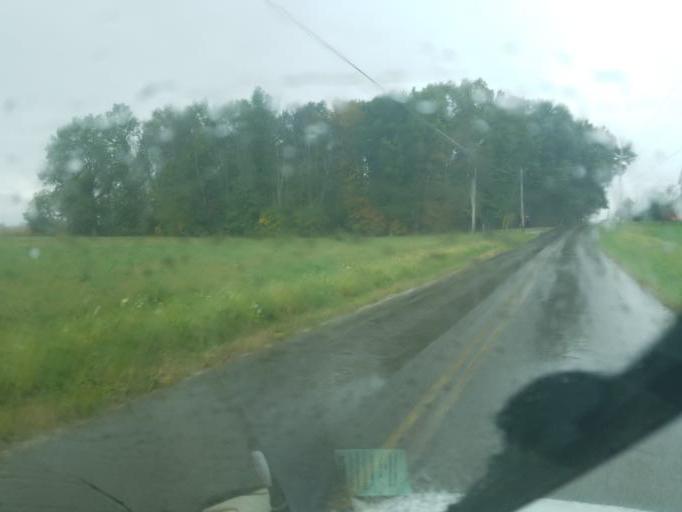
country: US
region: Ohio
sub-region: Wayne County
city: Shreve
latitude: 40.6453
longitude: -82.0211
